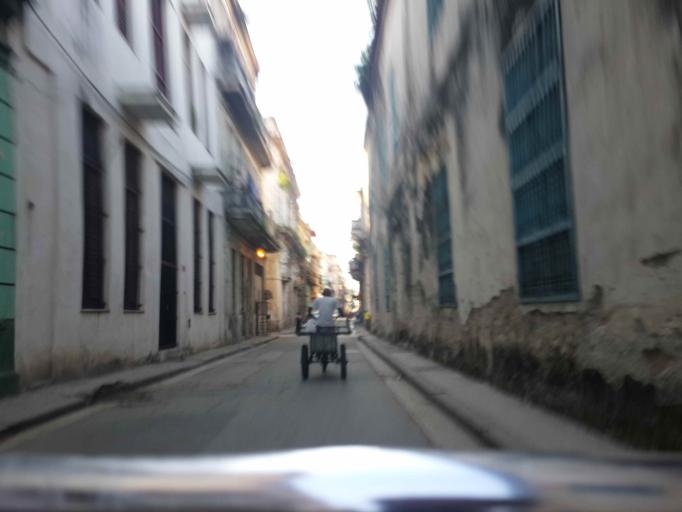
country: CU
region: La Habana
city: La Habana Vieja
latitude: 23.1340
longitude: -82.3506
